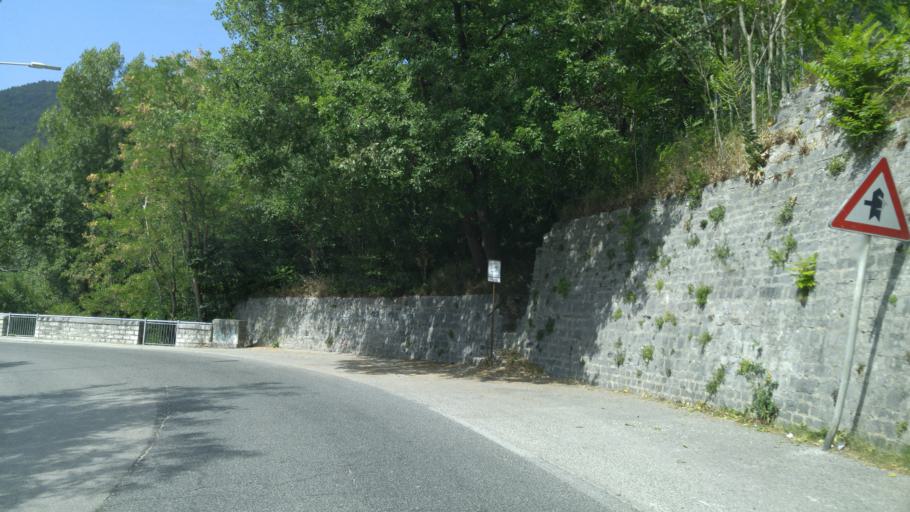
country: IT
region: The Marches
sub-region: Provincia di Pesaro e Urbino
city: Cagli
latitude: 43.5428
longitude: 12.6490
